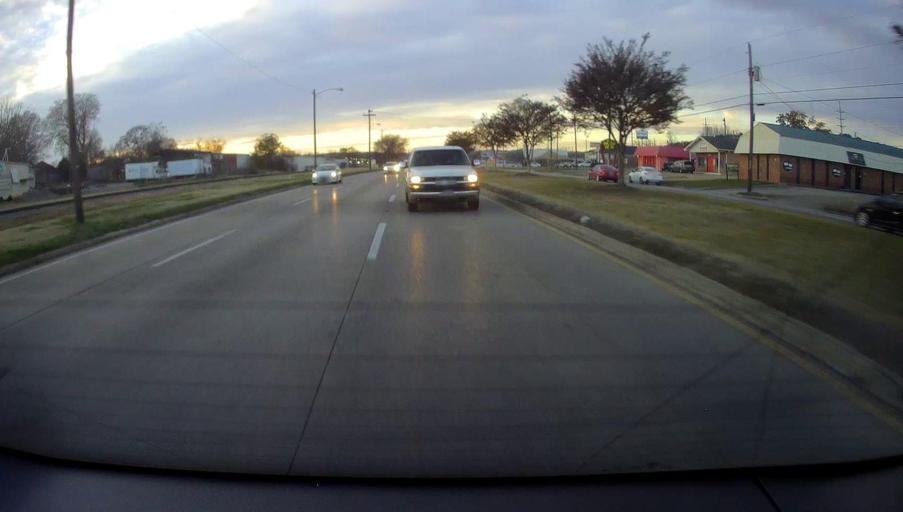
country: US
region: Alabama
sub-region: Etowah County
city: Gadsden
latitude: 34.0187
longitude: -86.0140
